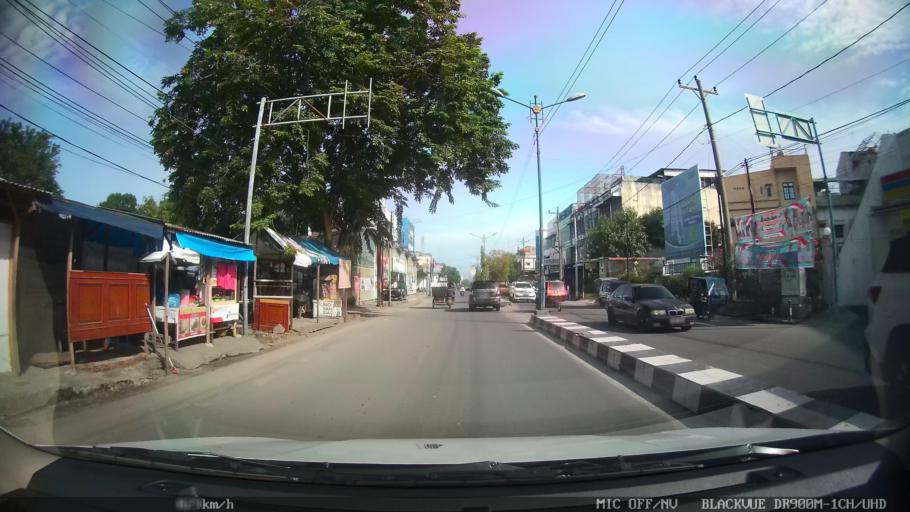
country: ID
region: North Sumatra
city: Medan
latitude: 3.5965
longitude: 98.6651
